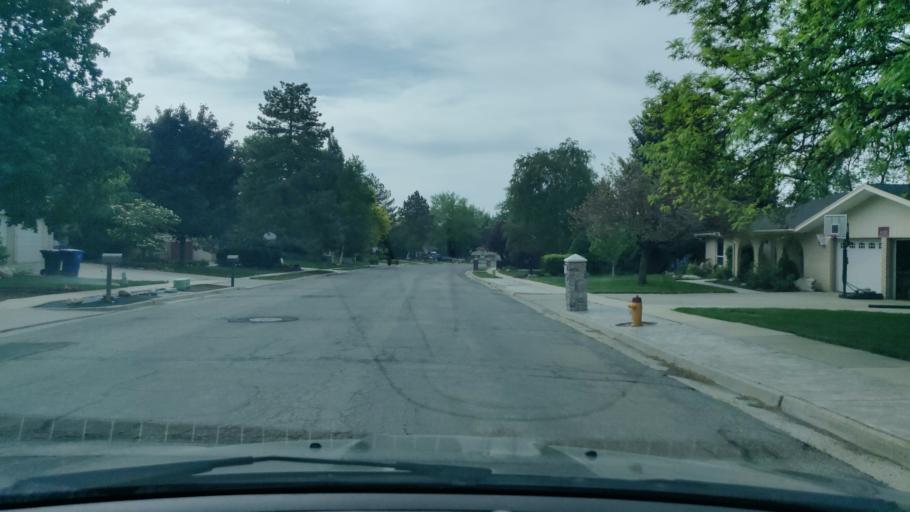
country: US
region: Utah
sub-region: Salt Lake County
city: Cottonwood Heights
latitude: 40.6189
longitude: -111.7974
